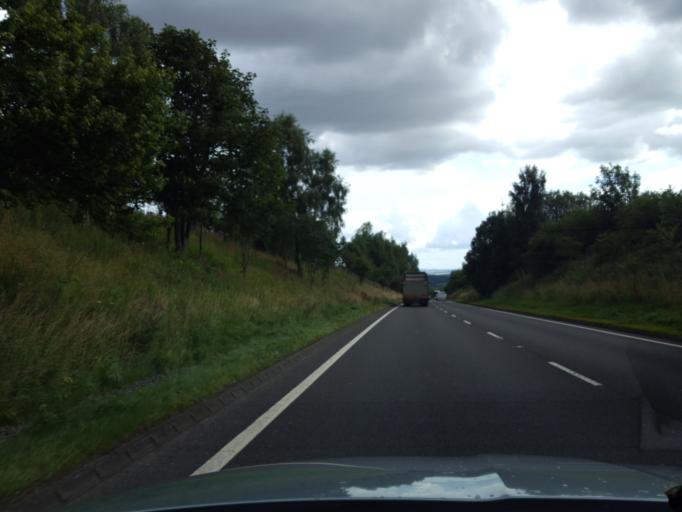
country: GB
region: Scotland
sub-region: Perth and Kinross
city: Bankfoot
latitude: 56.5058
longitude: -3.5110
